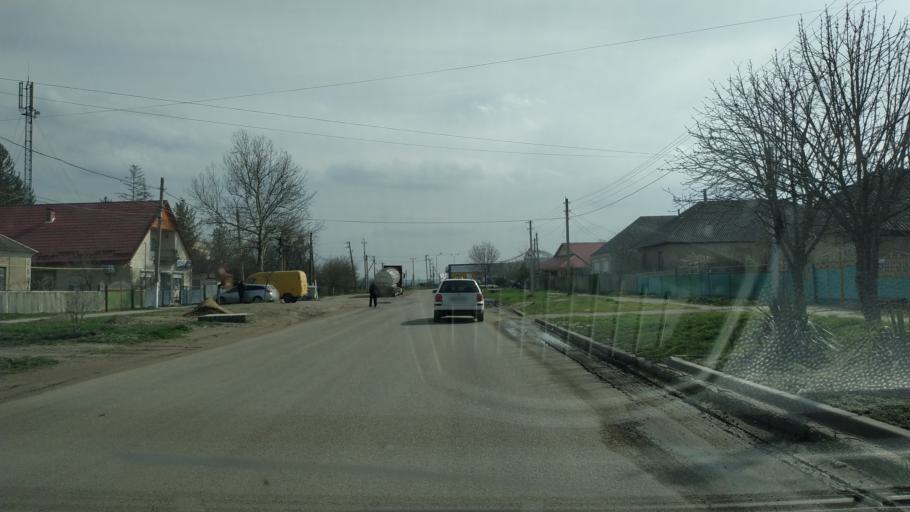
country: MD
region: Gagauzia
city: Vulcanesti
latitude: 45.6783
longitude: 28.4106
